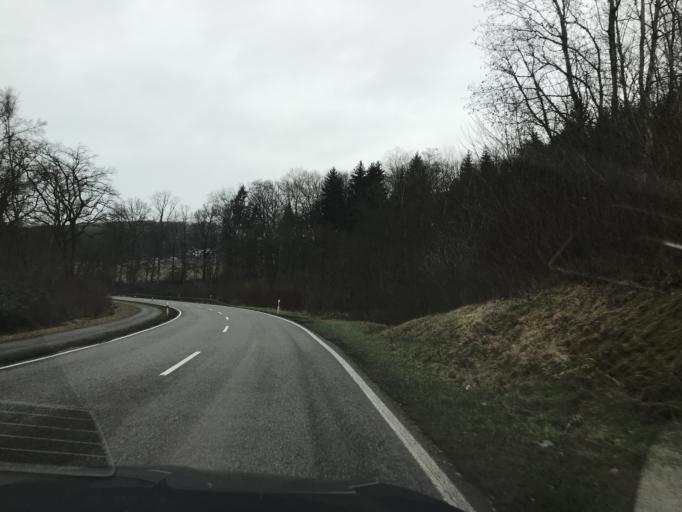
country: DE
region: Baden-Wuerttemberg
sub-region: Regierungsbezirk Stuttgart
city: Wolfschlugen
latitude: 48.6394
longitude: 9.3095
